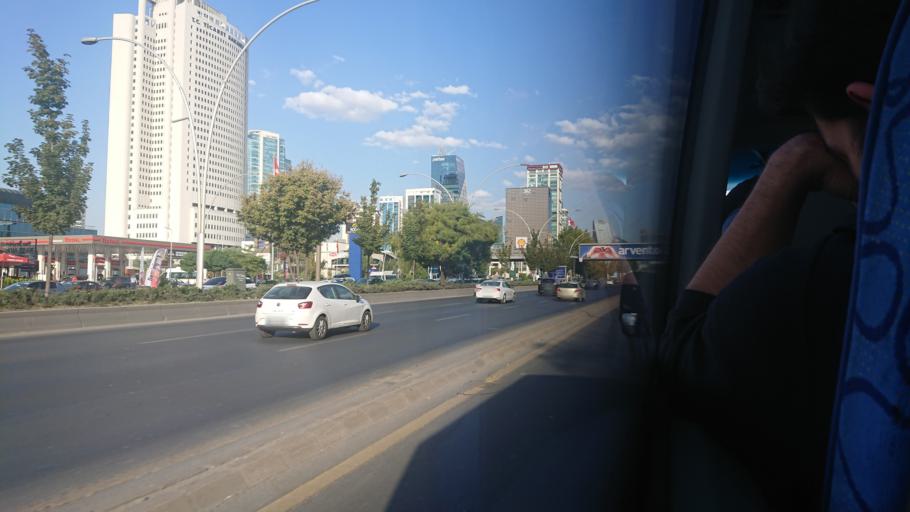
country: TR
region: Ankara
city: Ankara
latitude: 39.9087
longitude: 32.7908
